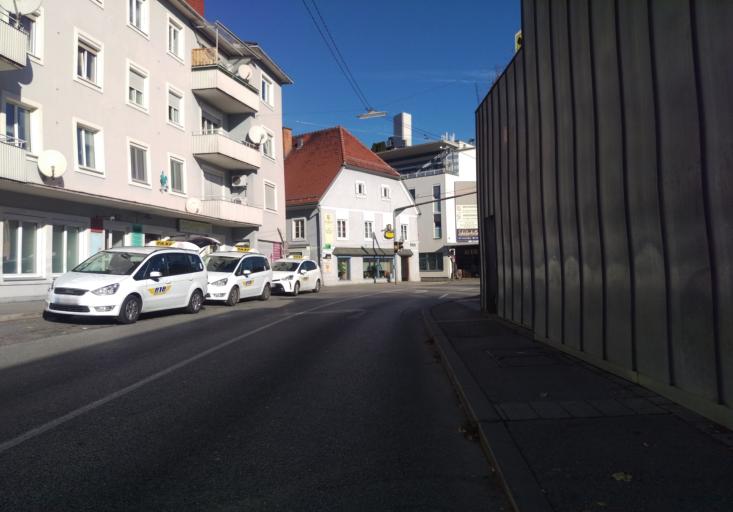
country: AT
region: Styria
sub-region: Graz Stadt
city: Goesting
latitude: 47.1032
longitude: 15.4212
